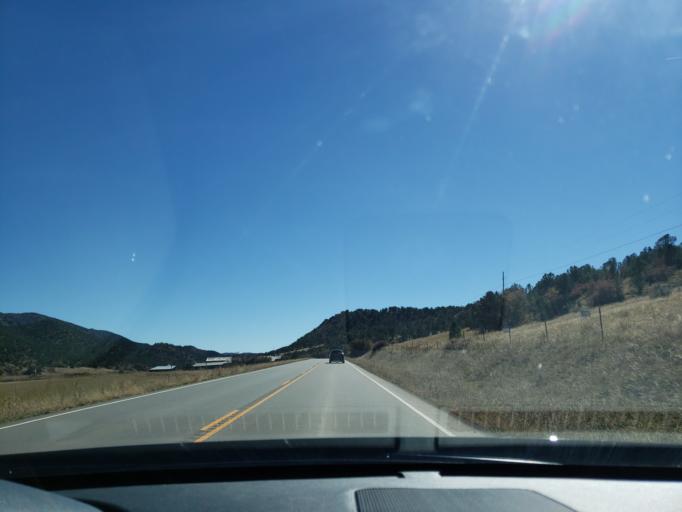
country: US
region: Colorado
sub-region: Fremont County
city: Canon City
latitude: 38.6068
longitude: -105.4373
